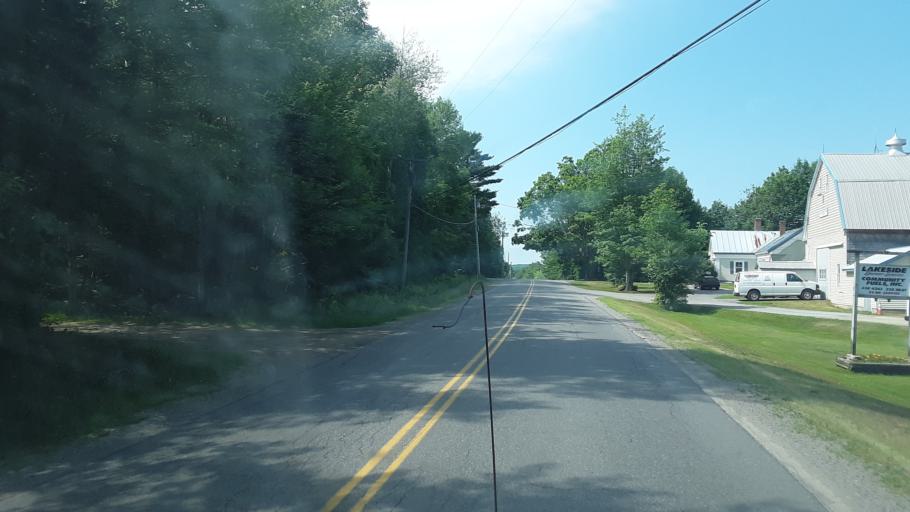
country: US
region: Maine
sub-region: Waldo County
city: Swanville
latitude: 44.5403
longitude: -68.9842
